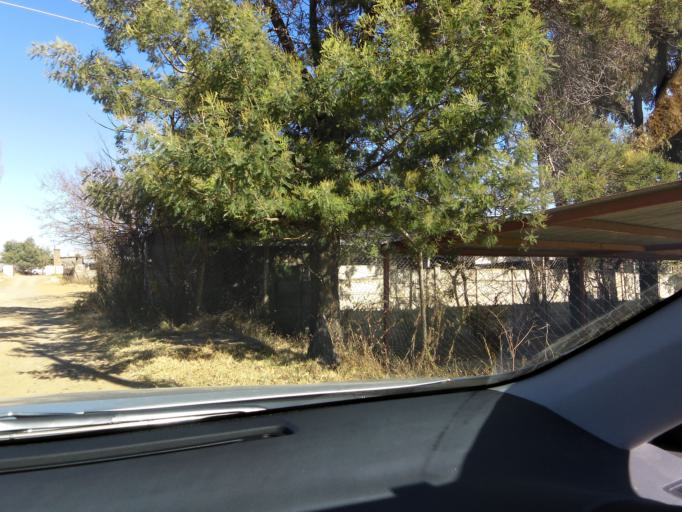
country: LS
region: Maseru
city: Maseru
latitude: -29.2843
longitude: 27.5278
